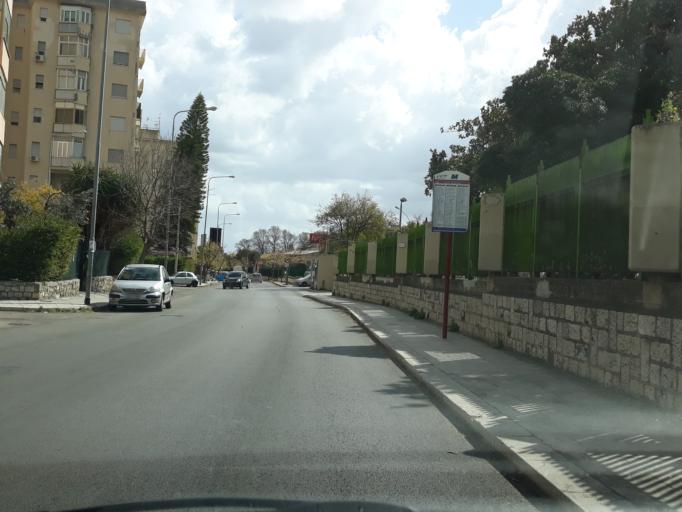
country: IT
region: Sicily
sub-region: Palermo
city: Palermo
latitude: 38.1234
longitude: 13.3199
